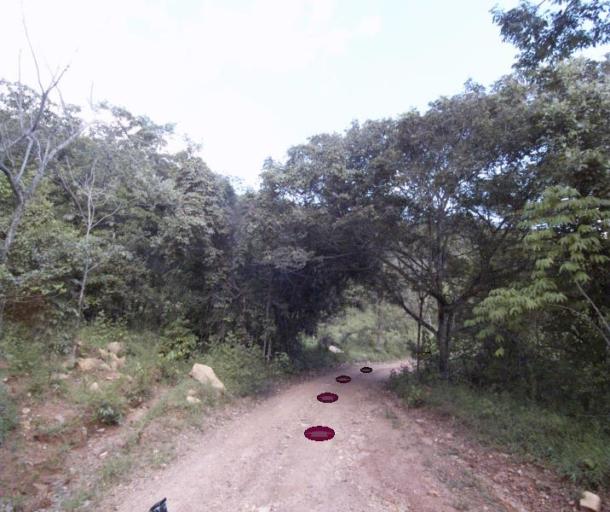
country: BR
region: Goias
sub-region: Pirenopolis
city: Pirenopolis
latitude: -15.7822
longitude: -48.9423
